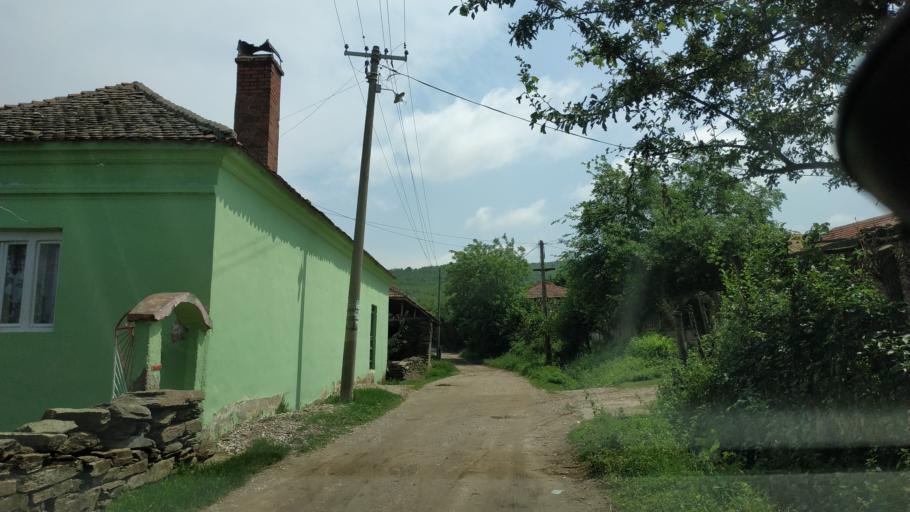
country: RS
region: Central Serbia
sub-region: Nisavski Okrug
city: Aleksinac
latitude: 43.4149
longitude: 21.7166
